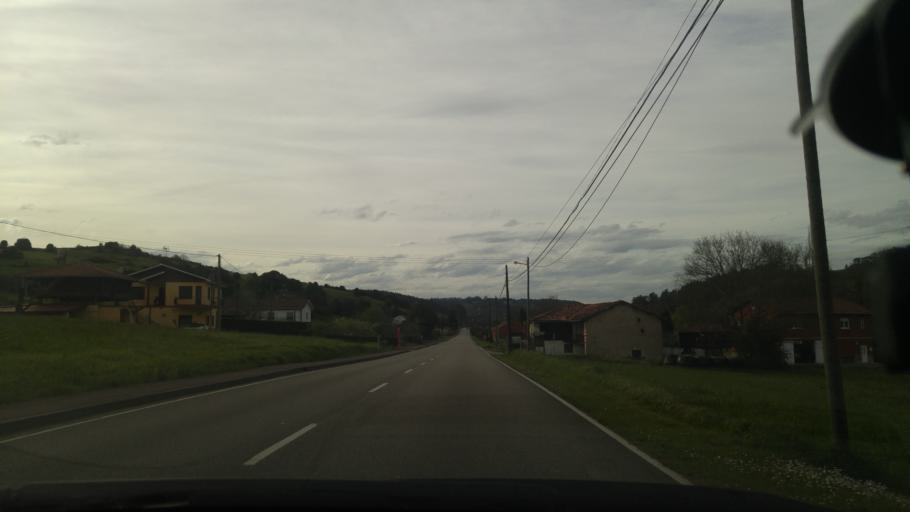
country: ES
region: Asturias
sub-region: Province of Asturias
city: Corvera de Asturias
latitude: 43.4918
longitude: -5.8500
